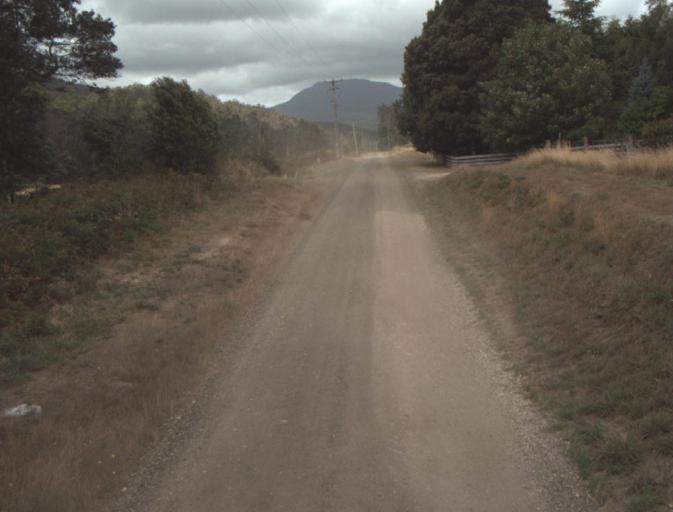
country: AU
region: Tasmania
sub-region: Dorset
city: Bridport
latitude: -41.1810
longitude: 147.2613
